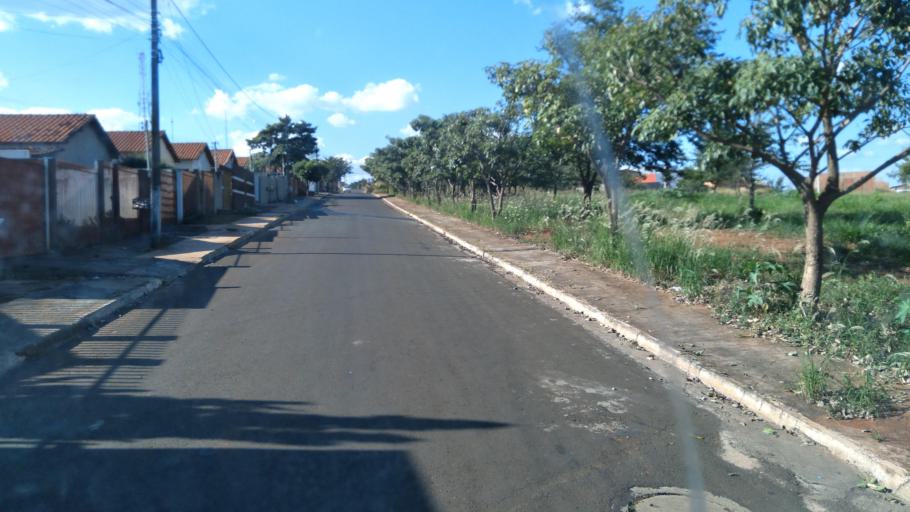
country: BR
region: Goias
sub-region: Mineiros
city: Mineiros
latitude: -17.5481
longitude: -52.5392
